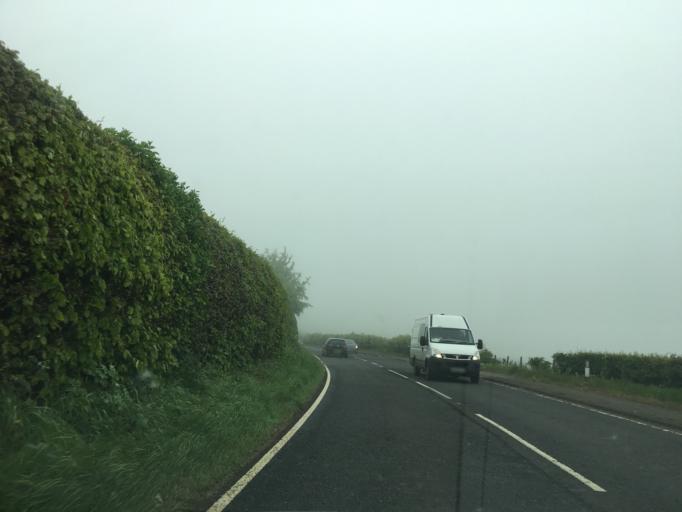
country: GB
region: Scotland
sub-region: Midlothian
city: Loanhead
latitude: 55.8820
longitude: -3.1940
